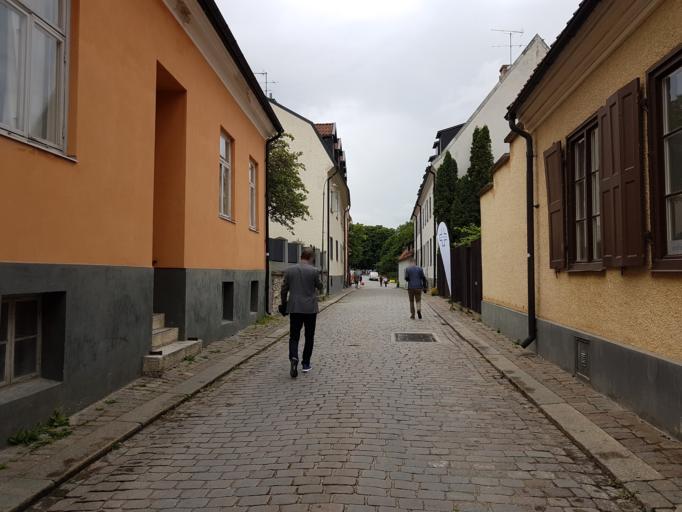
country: SE
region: Gotland
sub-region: Gotland
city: Visby
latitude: 57.6376
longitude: 18.2914
